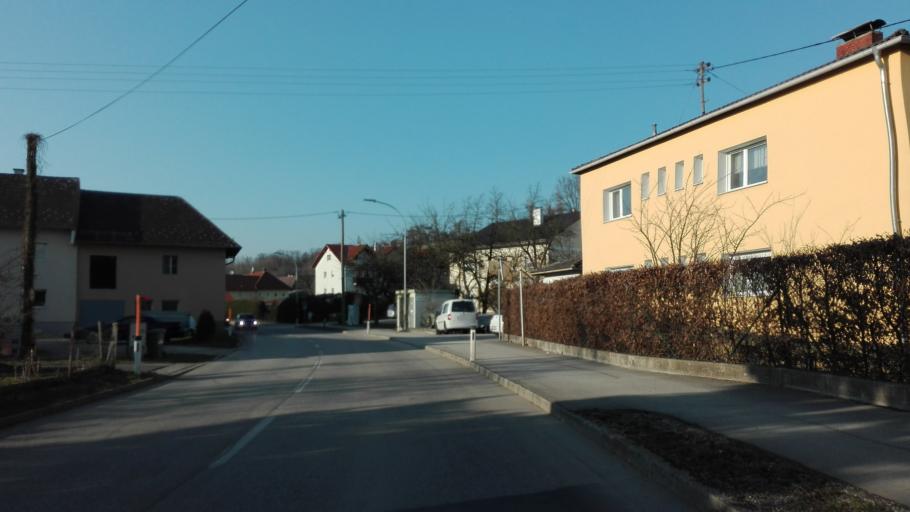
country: AT
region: Upper Austria
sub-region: Politischer Bezirk Linz-Land
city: Leonding
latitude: 48.2847
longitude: 14.2443
